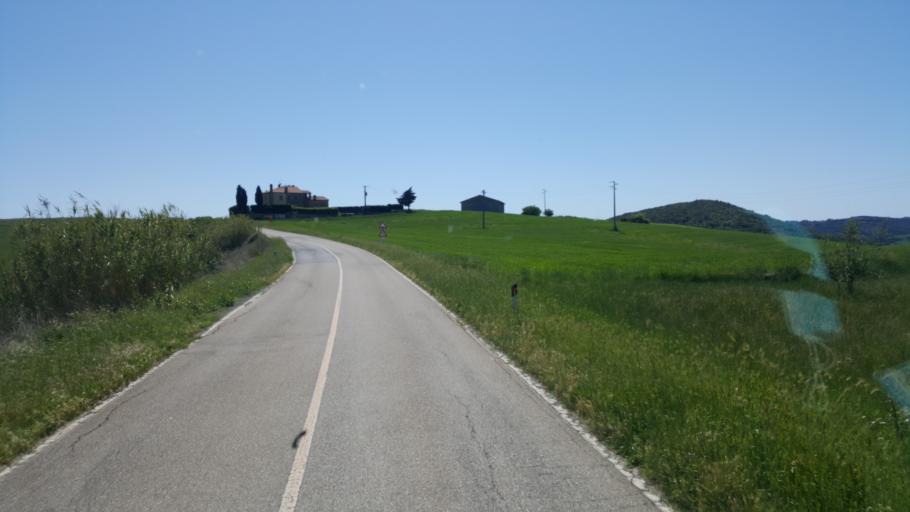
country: IT
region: Tuscany
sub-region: Province of Pisa
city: Castellina Marittima
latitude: 43.4230
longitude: 10.5271
